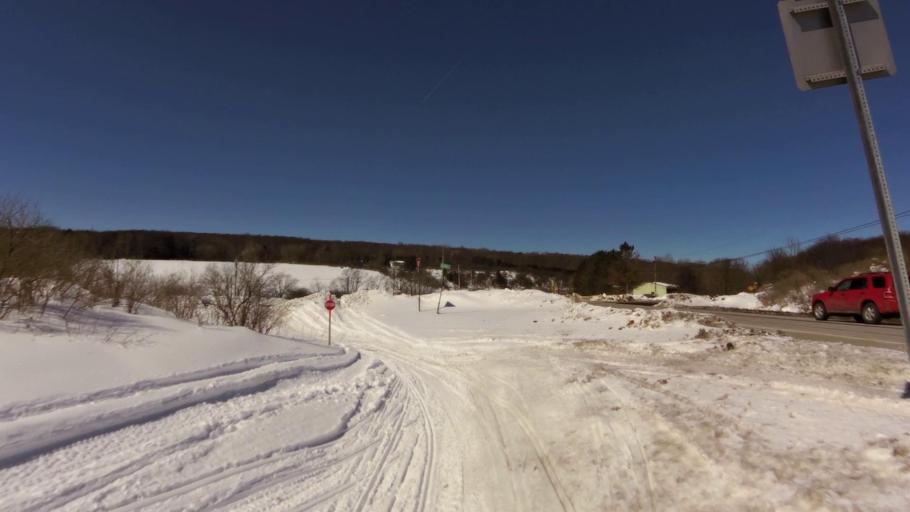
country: US
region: New York
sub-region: Wyoming County
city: Arcade
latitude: 42.4415
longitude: -78.3365
